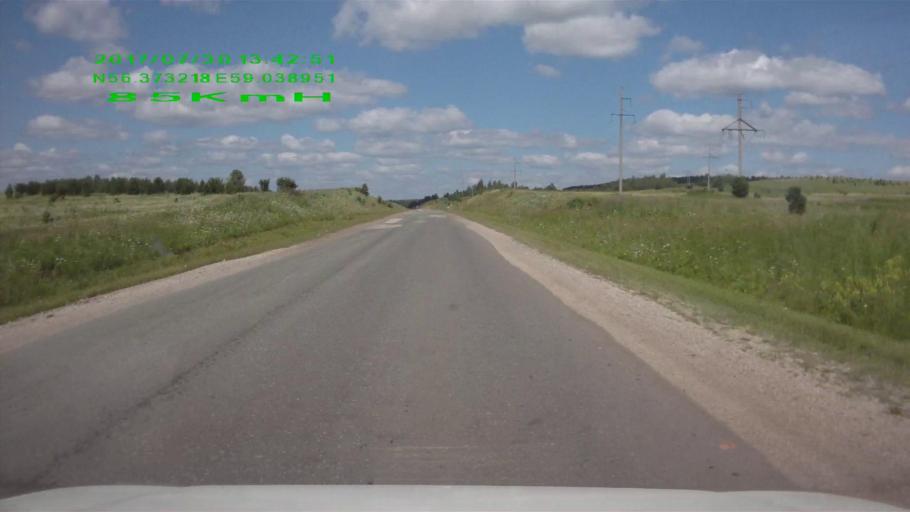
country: RU
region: Sverdlovsk
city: Mikhaylovsk
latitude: 56.3736
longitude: 59.0390
